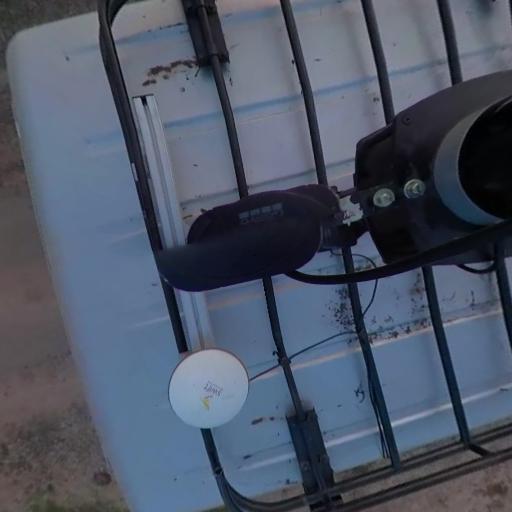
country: IN
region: Telangana
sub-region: Nalgonda
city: Suriapet
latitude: 17.0670
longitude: 79.5479
